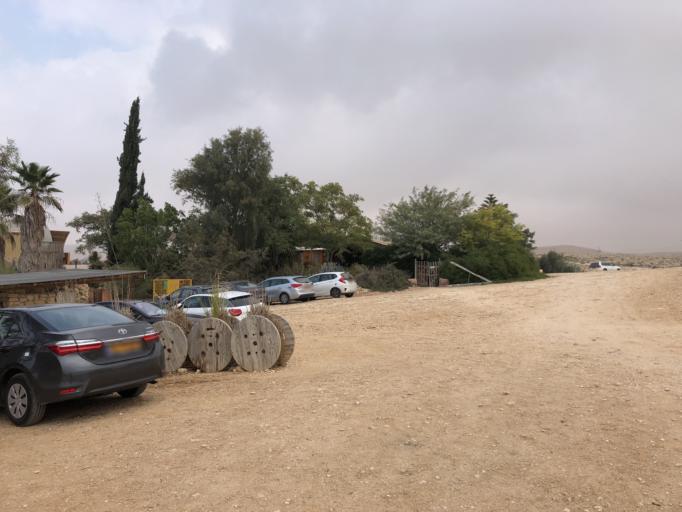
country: IL
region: Southern District
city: Midreshet Ben-Gurion
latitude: 30.9060
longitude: 34.7758
